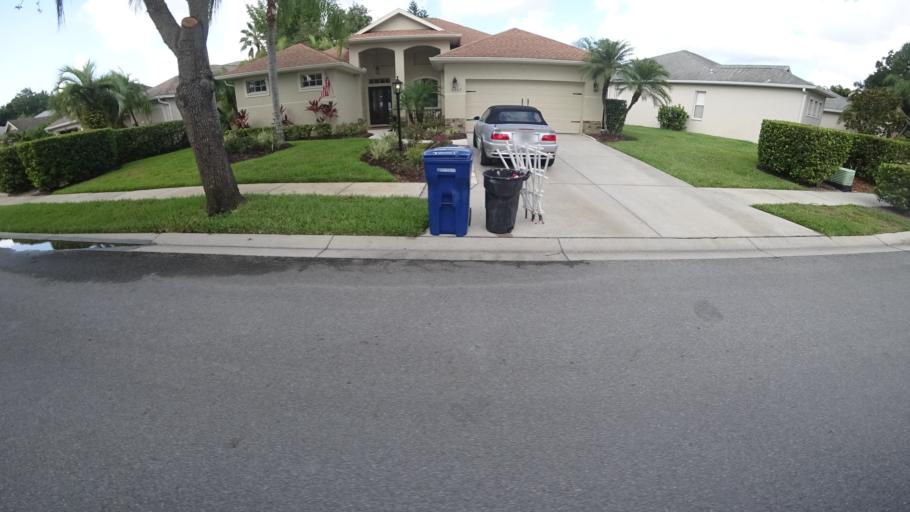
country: US
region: Florida
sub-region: Sarasota County
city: The Meadows
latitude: 27.4243
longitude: -82.4308
